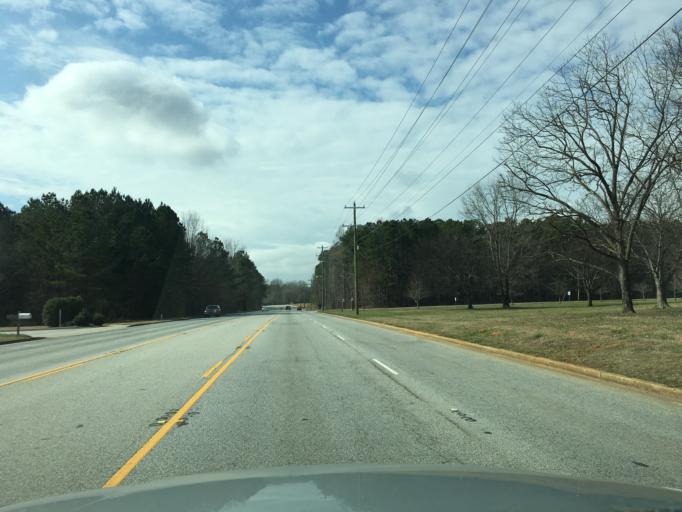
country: US
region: South Carolina
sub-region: Laurens County
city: Clinton
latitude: 34.4592
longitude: -81.8625
